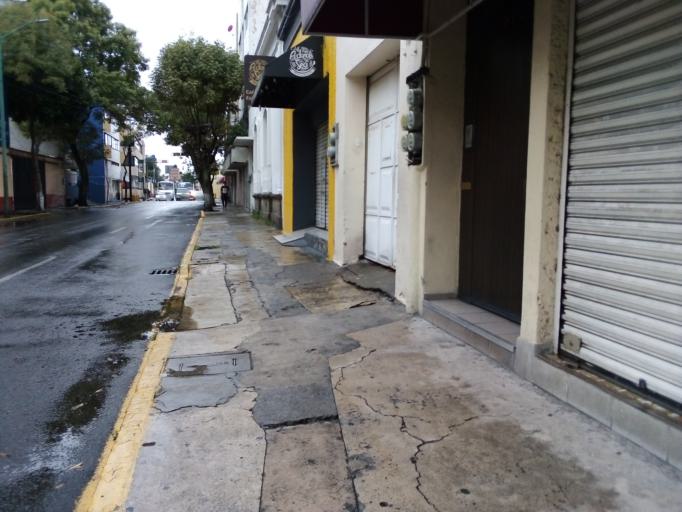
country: MX
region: Mexico
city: Toluca
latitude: 19.2870
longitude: -99.6577
